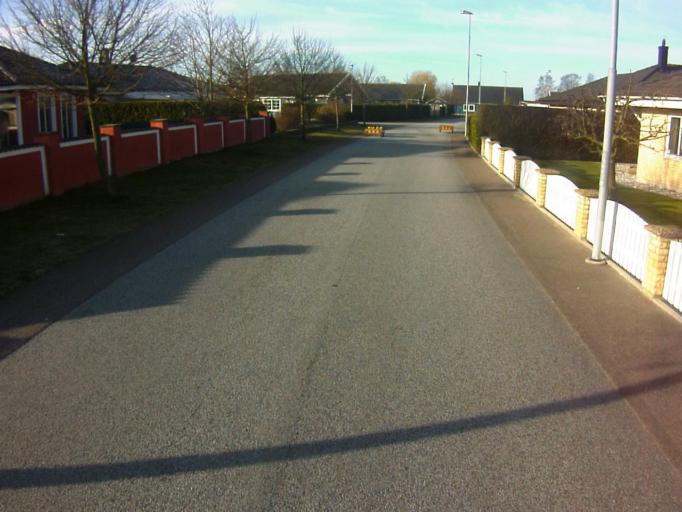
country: SE
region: Skane
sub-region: Kavlinge Kommun
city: Kaevlinge
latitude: 55.7954
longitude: 13.0908
